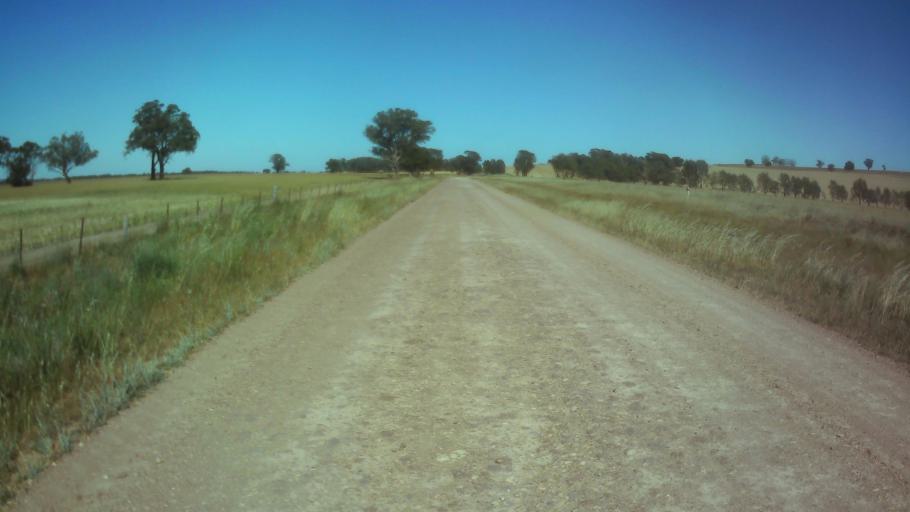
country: AU
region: New South Wales
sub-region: Weddin
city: Grenfell
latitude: -33.9951
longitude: 148.3602
